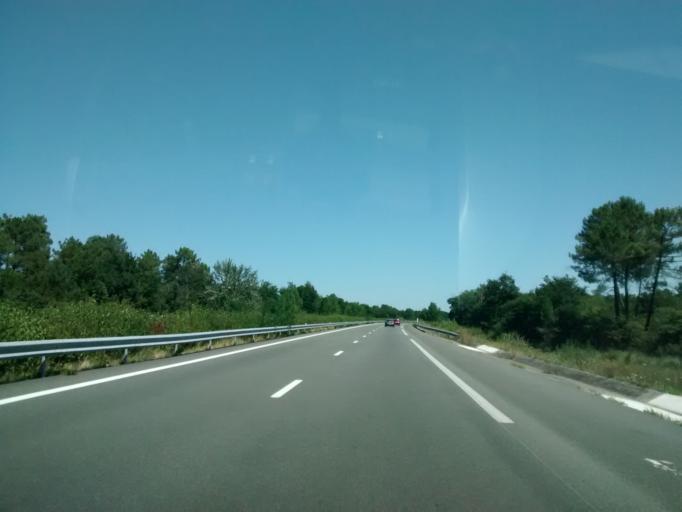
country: FR
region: Aquitaine
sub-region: Departement de la Dordogne
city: Le Pizou
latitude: 44.9885
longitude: 0.0899
